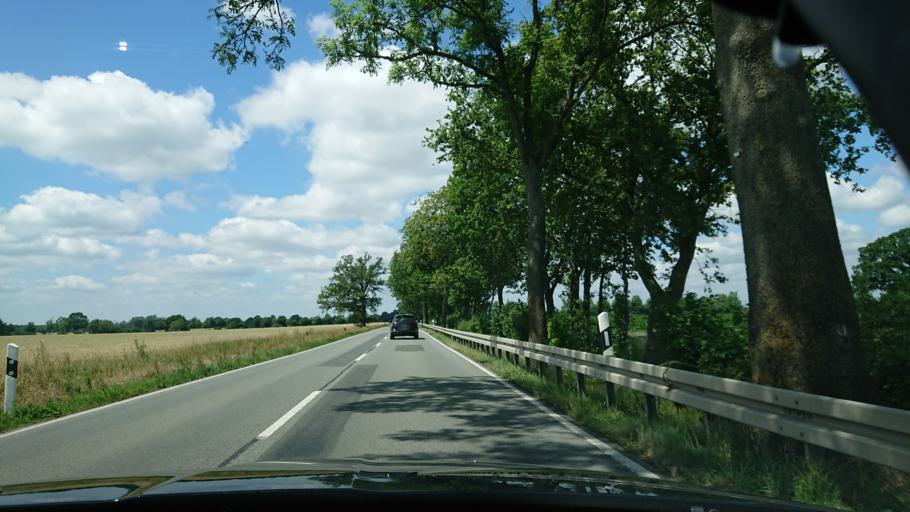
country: DE
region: Brandenburg
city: Perleberg
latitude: 53.0533
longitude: 11.9182
